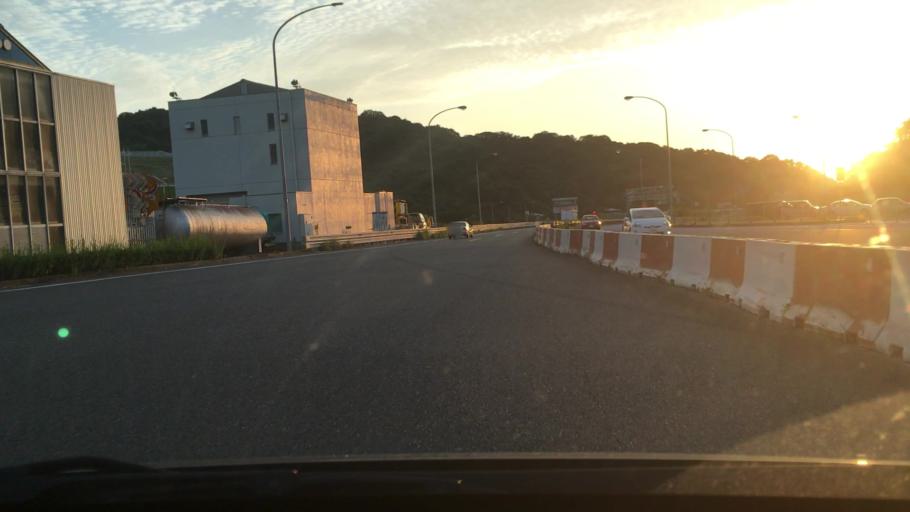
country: JP
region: Fukuoka
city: Maebaru-chuo
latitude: 33.5693
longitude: 130.2939
